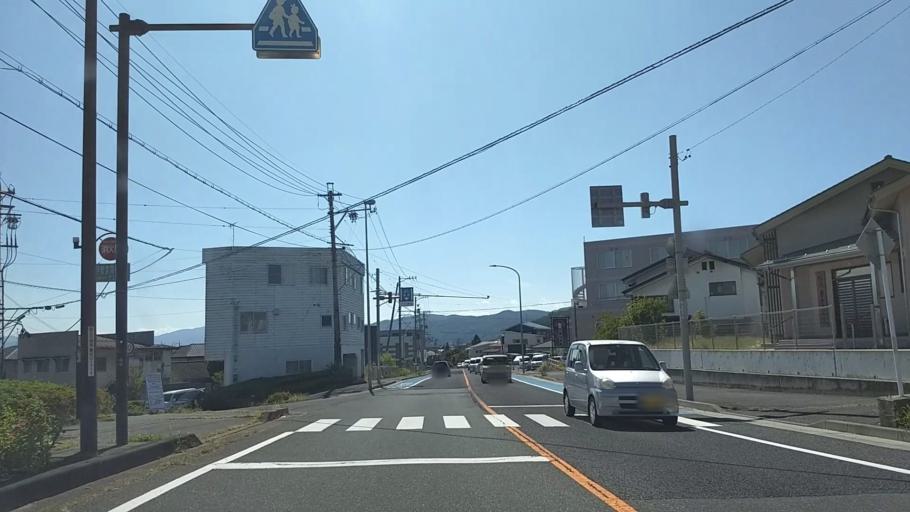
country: JP
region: Nagano
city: Nagano-shi
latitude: 36.6390
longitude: 138.1739
